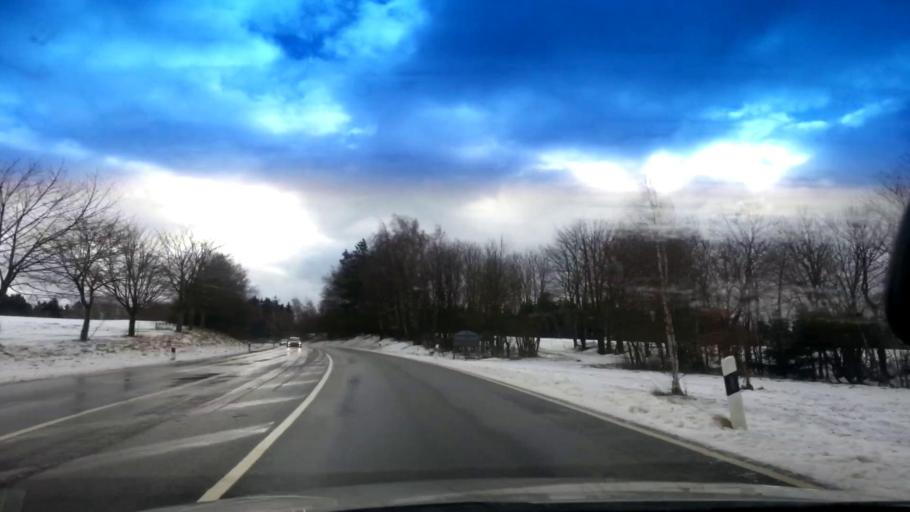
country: DE
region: Bavaria
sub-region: Upper Franconia
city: Kirchenlamitz
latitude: 50.1472
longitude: 11.9600
